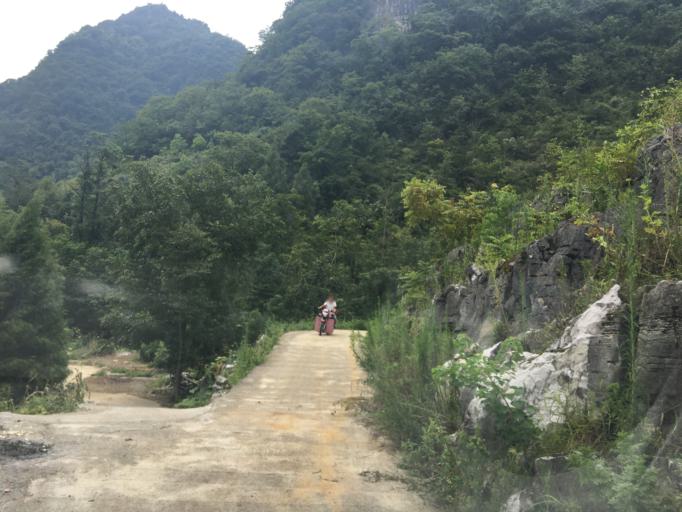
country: CN
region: Guangxi Zhuangzu Zizhiqu
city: Xinzhou
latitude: 25.2262
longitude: 105.6368
